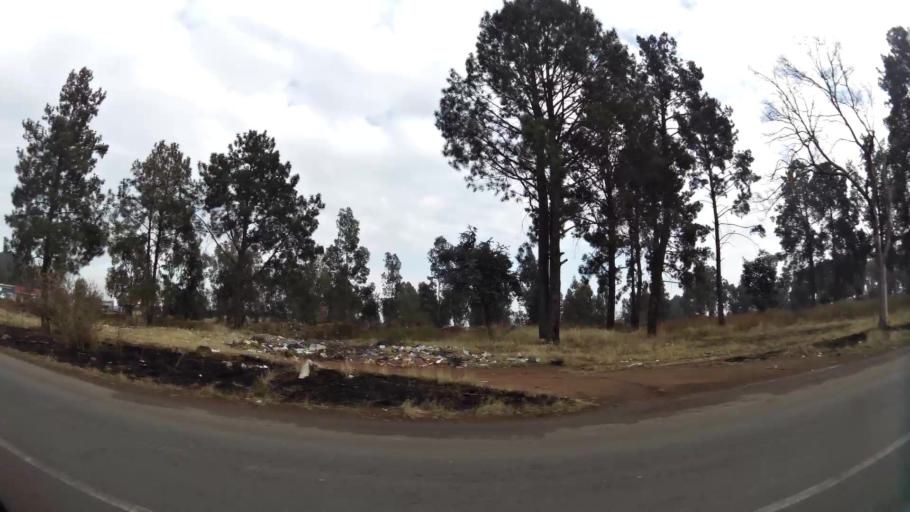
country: ZA
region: Gauteng
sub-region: Sedibeng District Municipality
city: Vanderbijlpark
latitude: -26.6939
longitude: 27.8114
